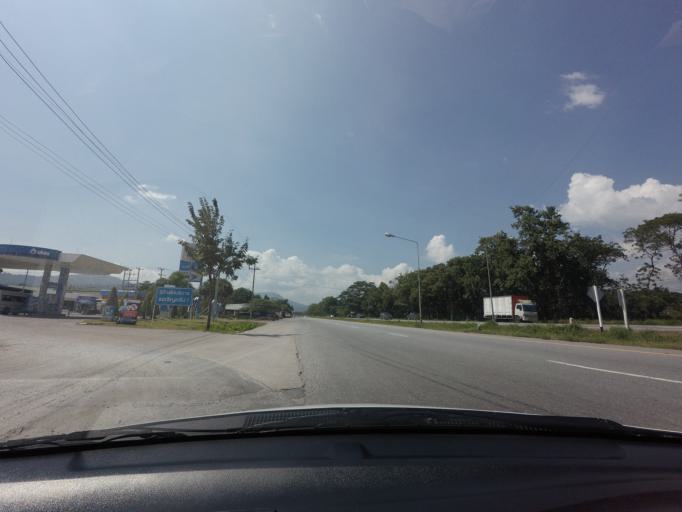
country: TH
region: Prachin Buri
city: Na Di
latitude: 14.2169
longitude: 101.9000
